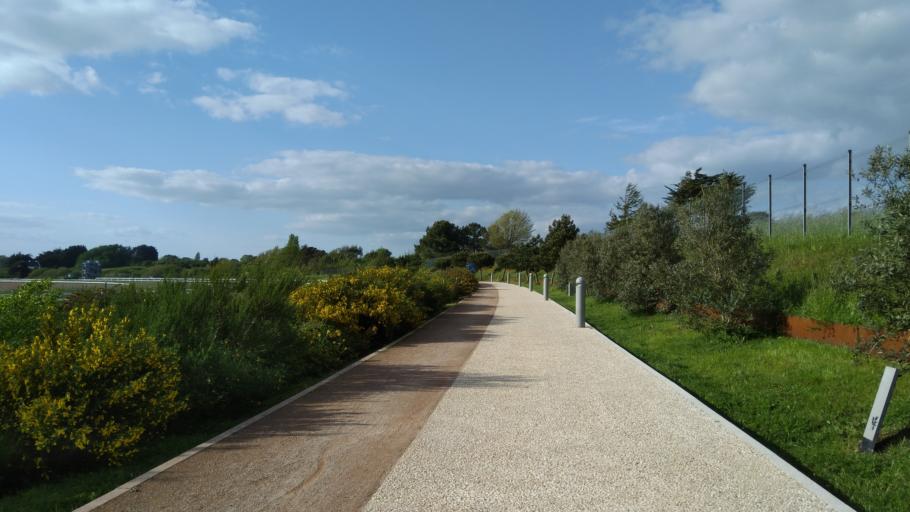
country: FR
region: Pays de la Loire
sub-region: Departement de la Loire-Atlantique
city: Pornichet
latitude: 47.2605
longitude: -2.3265
